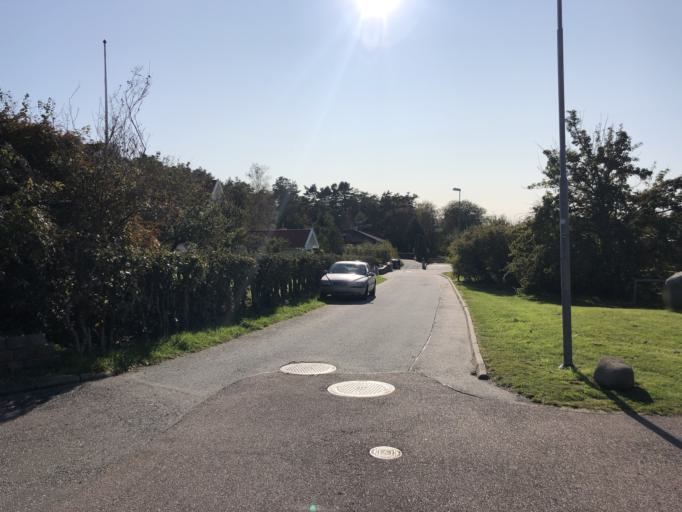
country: SE
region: Vaestra Goetaland
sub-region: Goteborg
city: Billdal
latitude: 57.6190
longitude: 11.8884
